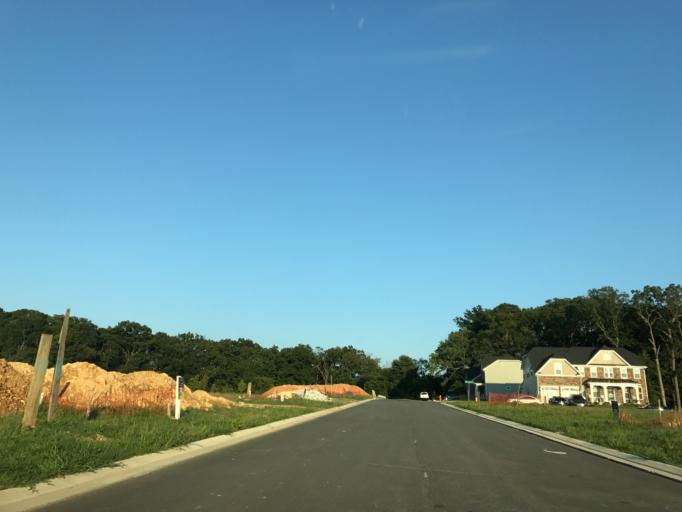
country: US
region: Maryland
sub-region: Baltimore County
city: Perry Hall
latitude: 39.4193
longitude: -76.4505
